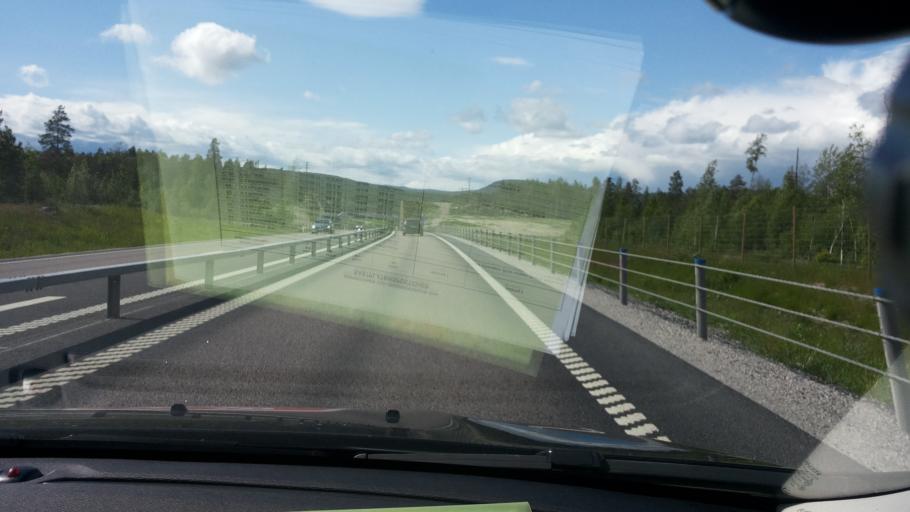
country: SE
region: Vaesternorrland
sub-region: Sundsvalls Kommun
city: Njurundabommen
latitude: 62.2611
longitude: 17.3634
